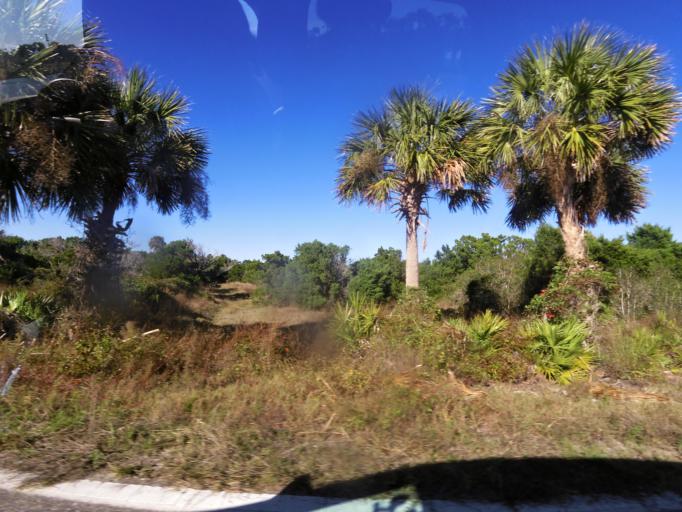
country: US
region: Florida
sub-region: Duval County
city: Atlantic Beach
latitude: 30.4242
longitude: -81.4127
